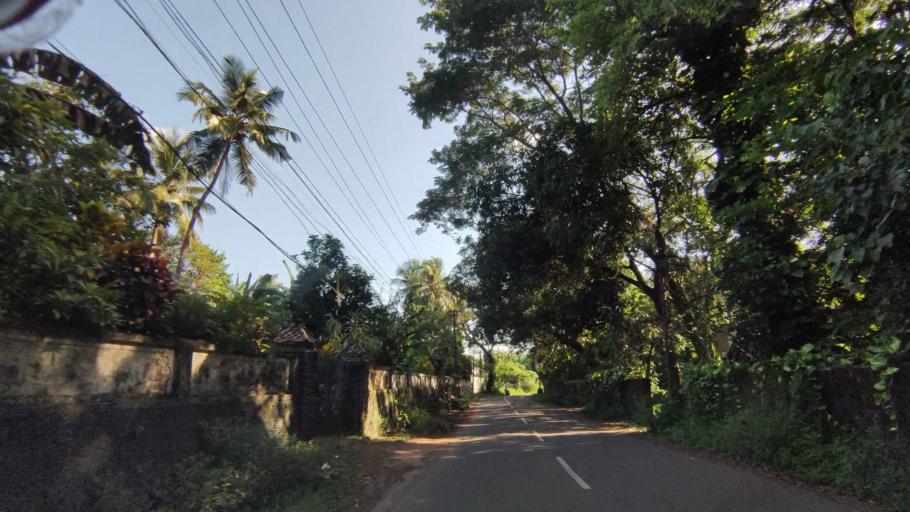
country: IN
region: Kerala
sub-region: Kottayam
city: Kottayam
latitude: 9.5586
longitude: 76.5112
